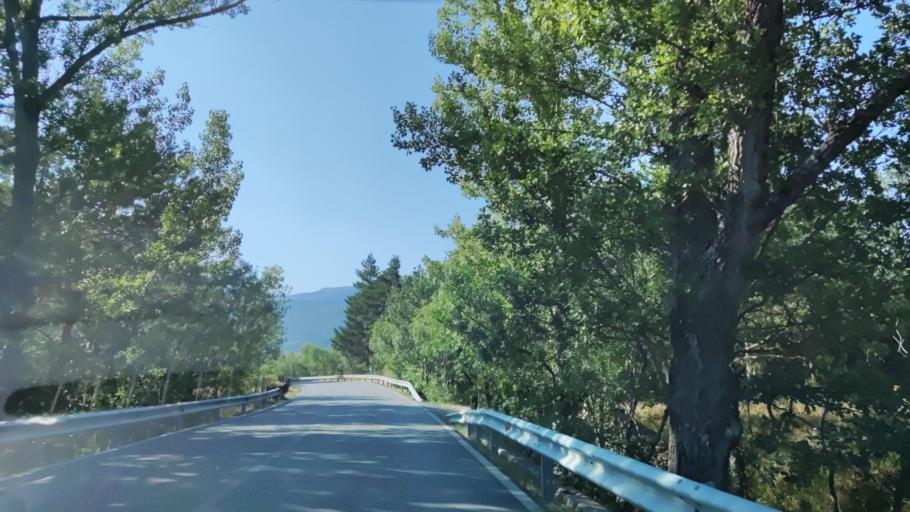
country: ES
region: Madrid
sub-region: Provincia de Madrid
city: Rascafria
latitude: 40.8812
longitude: -3.8849
